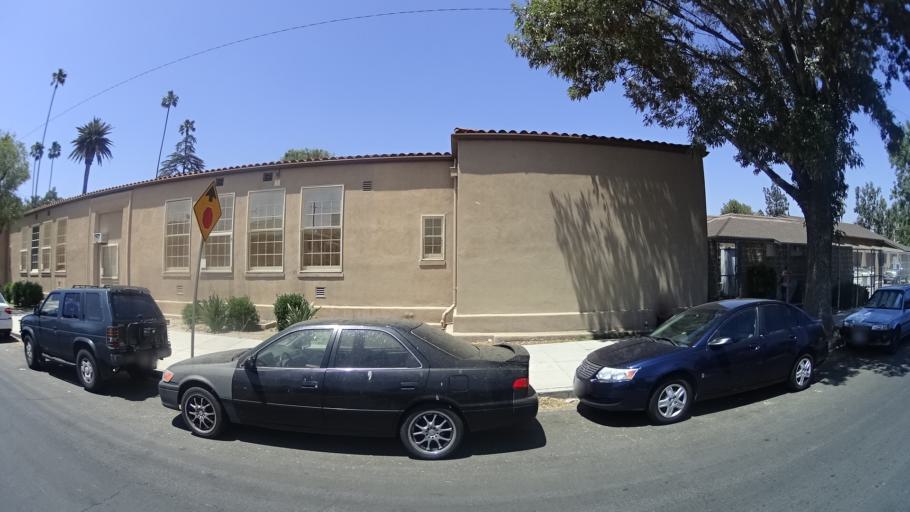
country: US
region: California
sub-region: Los Angeles County
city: Van Nuys
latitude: 34.1876
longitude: -118.4458
